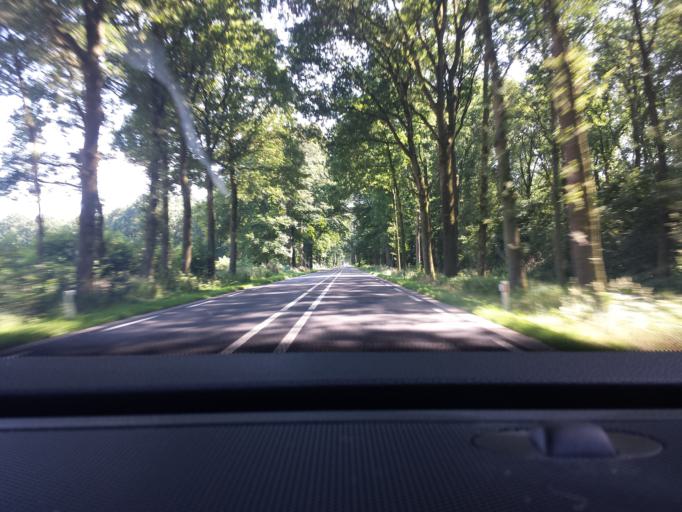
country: NL
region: Gelderland
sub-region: Gemeente Bronckhorst
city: Baak
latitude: 52.0260
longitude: 6.2177
